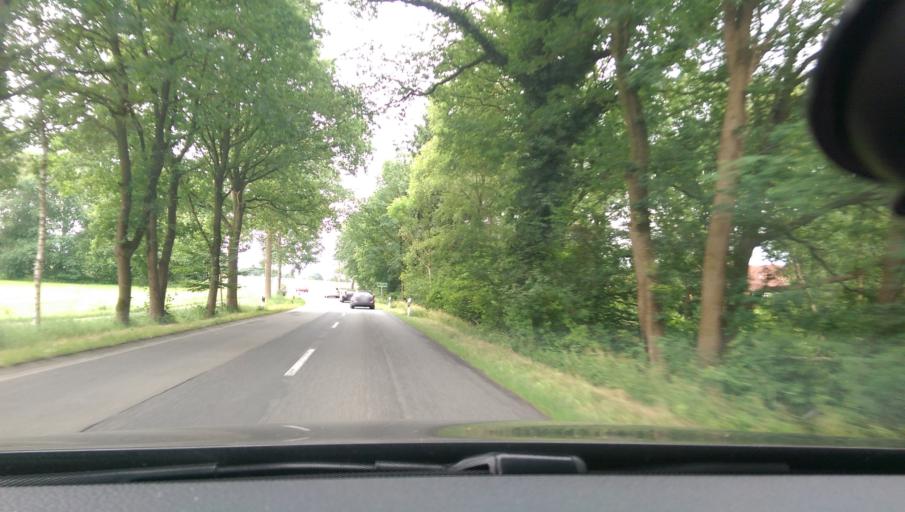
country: DE
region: Lower Saxony
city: Horstedt
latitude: 53.1763
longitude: 9.2659
